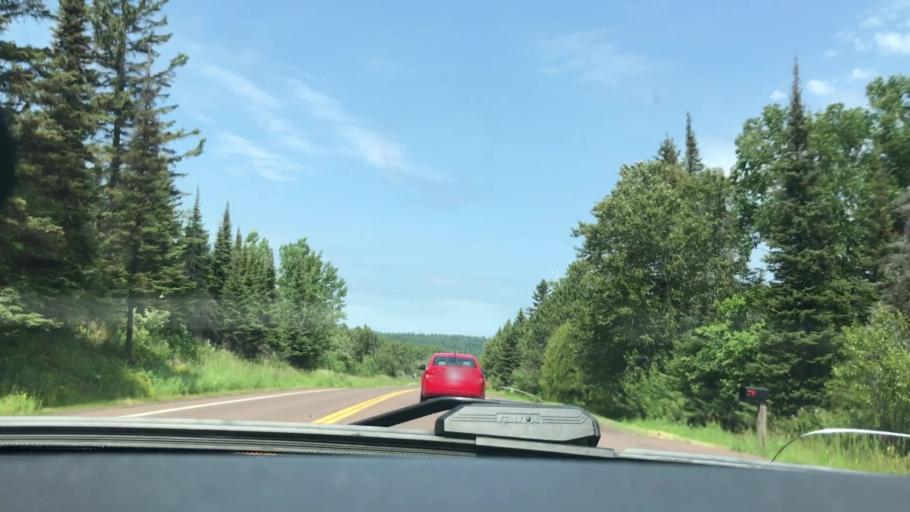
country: US
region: Minnesota
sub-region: Lake County
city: Two Harbors
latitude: 47.0773
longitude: -91.5860
